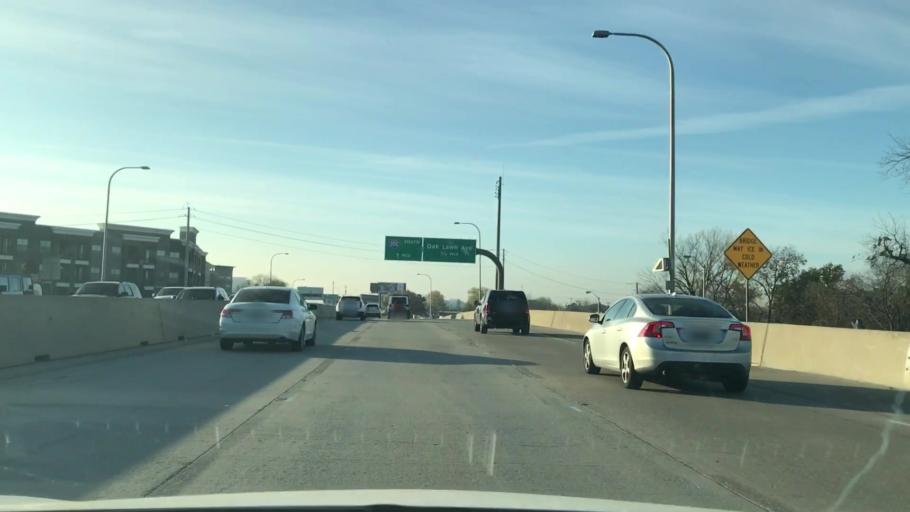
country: US
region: Texas
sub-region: Dallas County
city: Dallas
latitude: 32.8124
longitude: -96.8180
